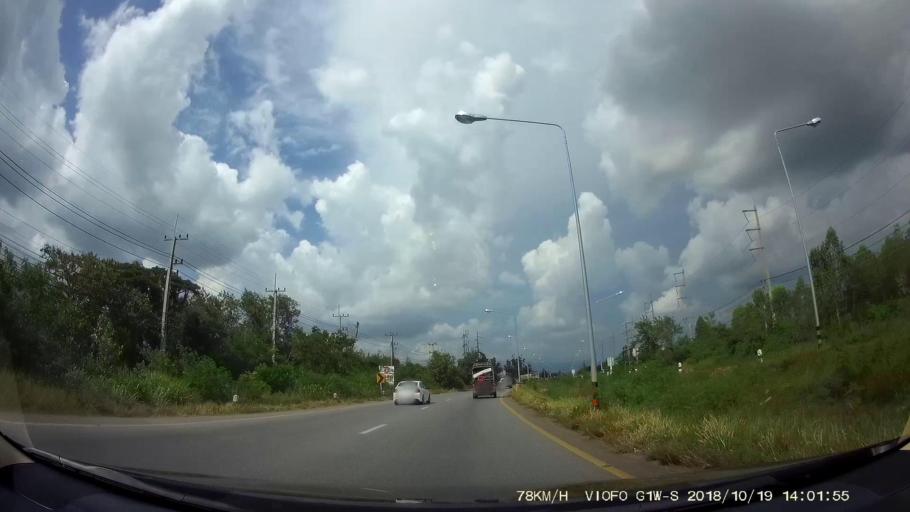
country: TH
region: Chaiyaphum
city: Chaiyaphum
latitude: 15.8350
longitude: 102.0585
